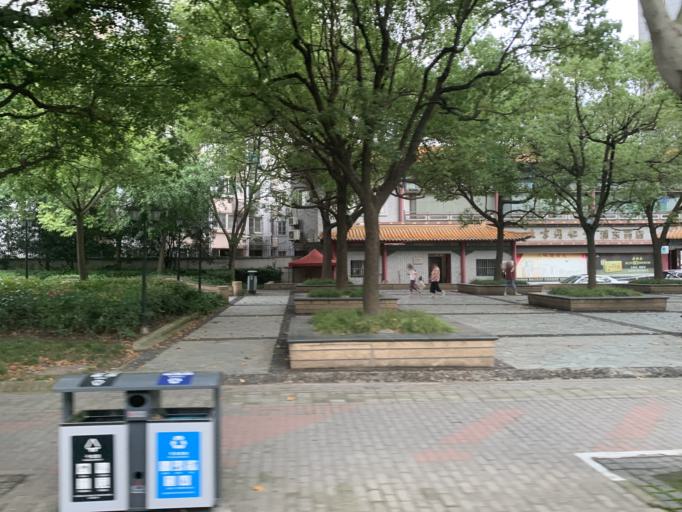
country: CN
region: Shanghai Shi
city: Pudong
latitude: 31.2341
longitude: 121.5197
